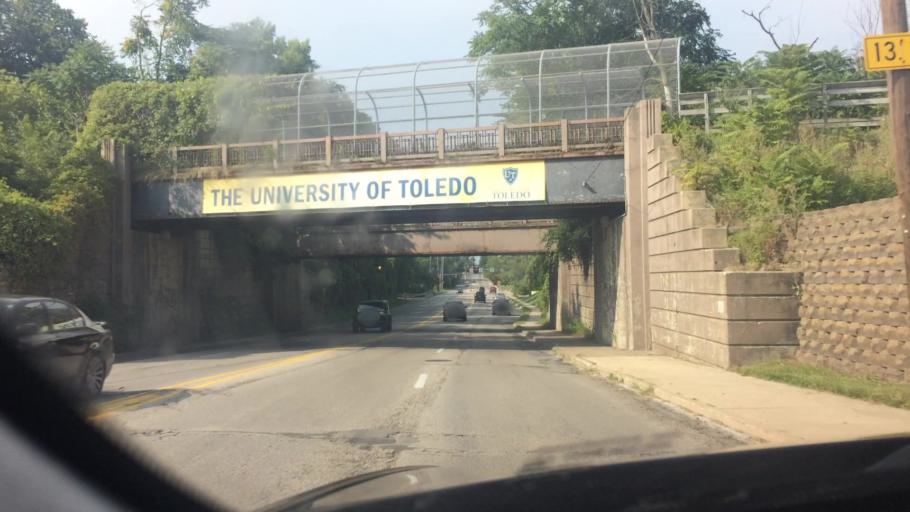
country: US
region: Ohio
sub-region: Lucas County
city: Ottawa Hills
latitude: 41.6561
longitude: -83.6219
